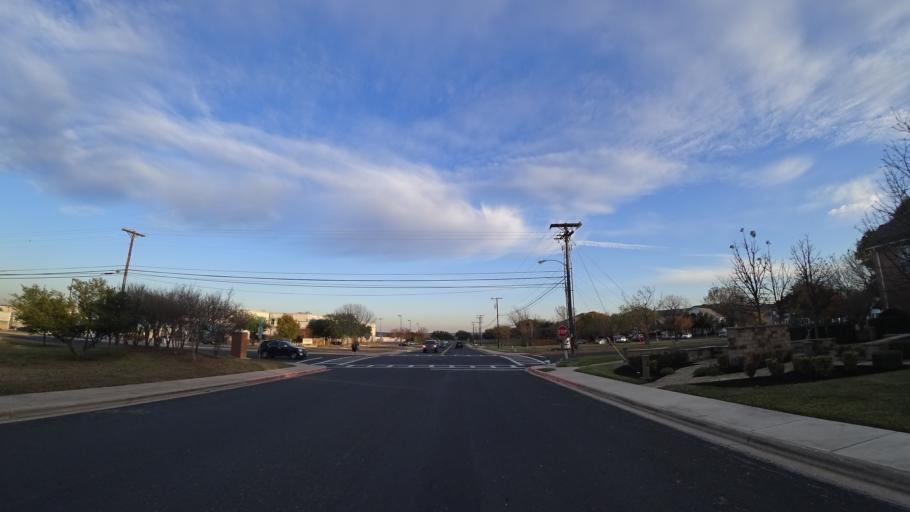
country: US
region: Texas
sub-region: Williamson County
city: Brushy Creek
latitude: 30.4921
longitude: -97.7357
